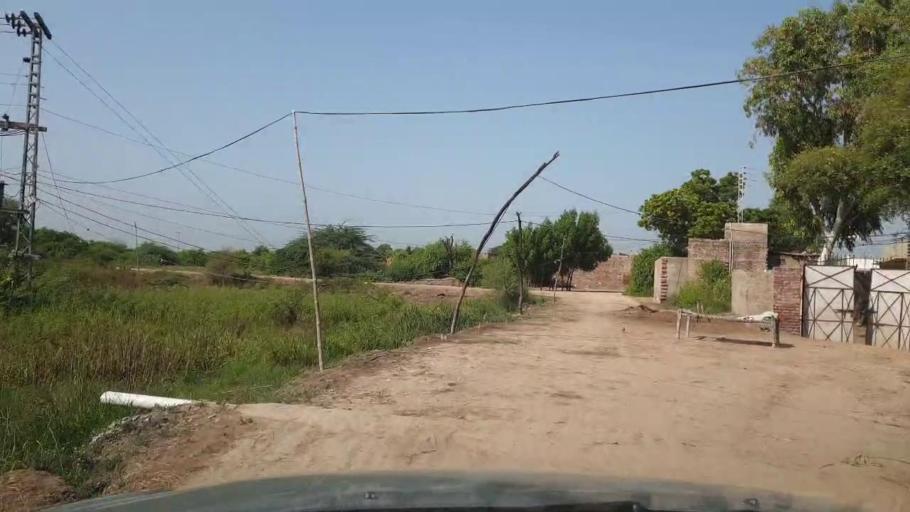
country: PK
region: Sindh
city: Tando Ghulam Ali
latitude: 25.1328
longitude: 68.8719
